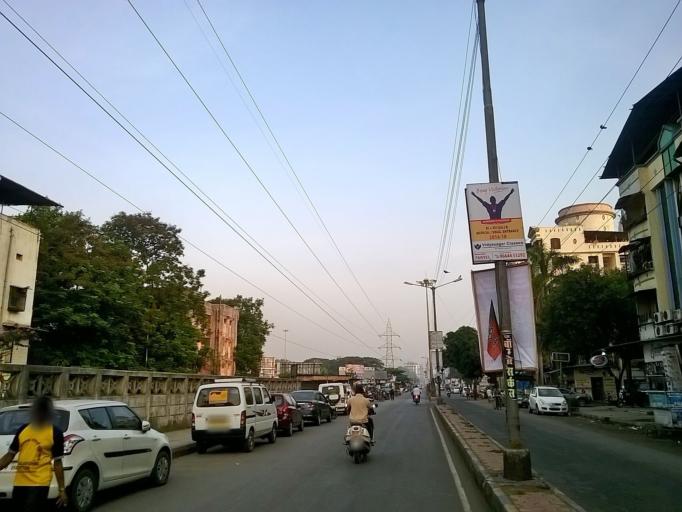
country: IN
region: Maharashtra
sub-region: Raigarh
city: Kalundri
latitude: 18.9908
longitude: 73.1243
